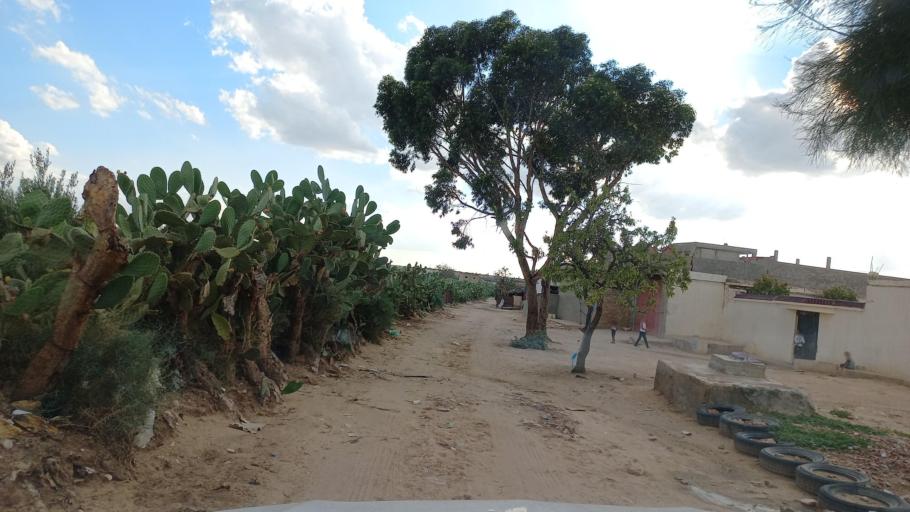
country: TN
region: Al Qasrayn
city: Sbiba
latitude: 35.3859
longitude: 9.0561
